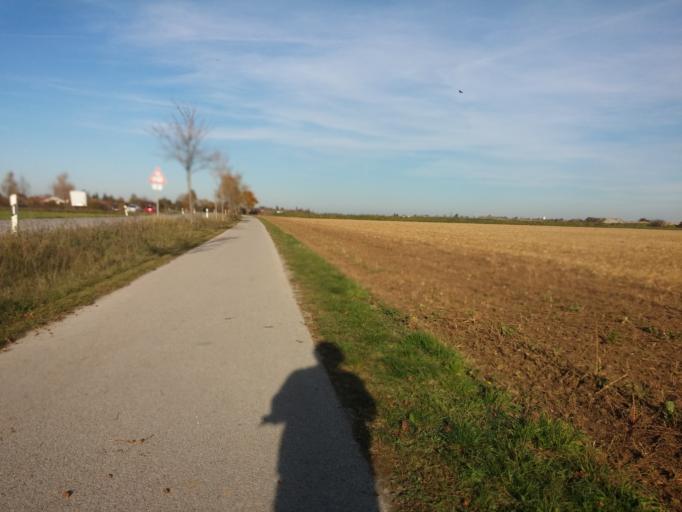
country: DE
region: Bavaria
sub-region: Upper Bavaria
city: Haar
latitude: 48.1232
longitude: 11.7125
